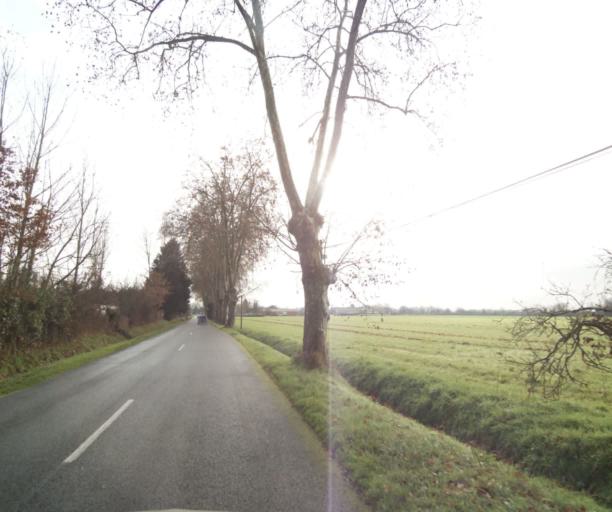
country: FR
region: Midi-Pyrenees
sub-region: Departement de la Haute-Garonne
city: Villemur-sur-Tarn
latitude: 43.8772
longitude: 1.4869
